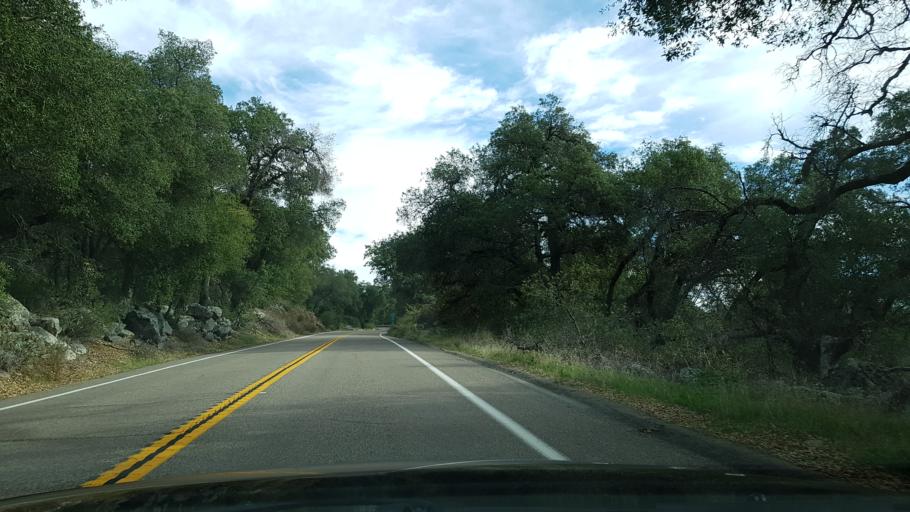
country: US
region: California
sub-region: Riverside County
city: Aguanga
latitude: 33.2944
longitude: -116.8919
